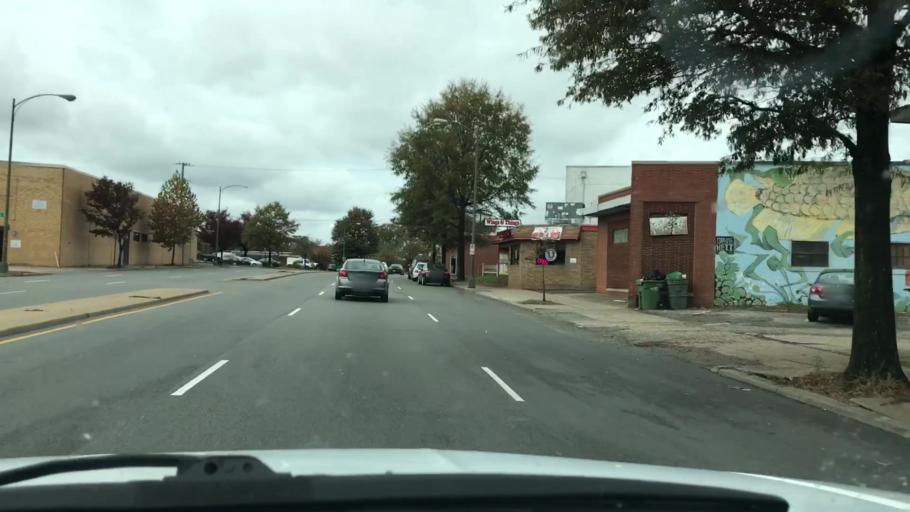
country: US
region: Virginia
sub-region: City of Richmond
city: Richmond
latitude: 37.5566
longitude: -77.4422
